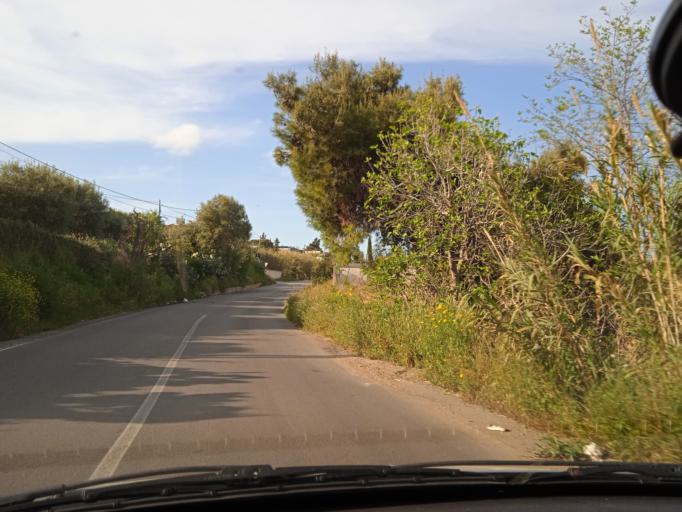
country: IT
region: Sicily
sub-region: Palermo
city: Portella di Mare
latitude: 38.0529
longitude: 13.4614
